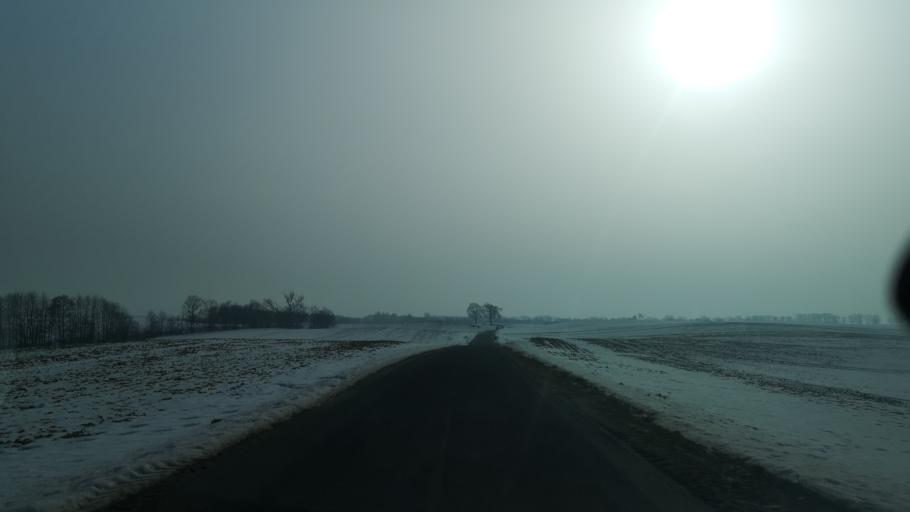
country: PL
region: Warmian-Masurian Voivodeship
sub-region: Powiat nowomiejski
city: Biskupiec
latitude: 53.5378
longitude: 19.3554
